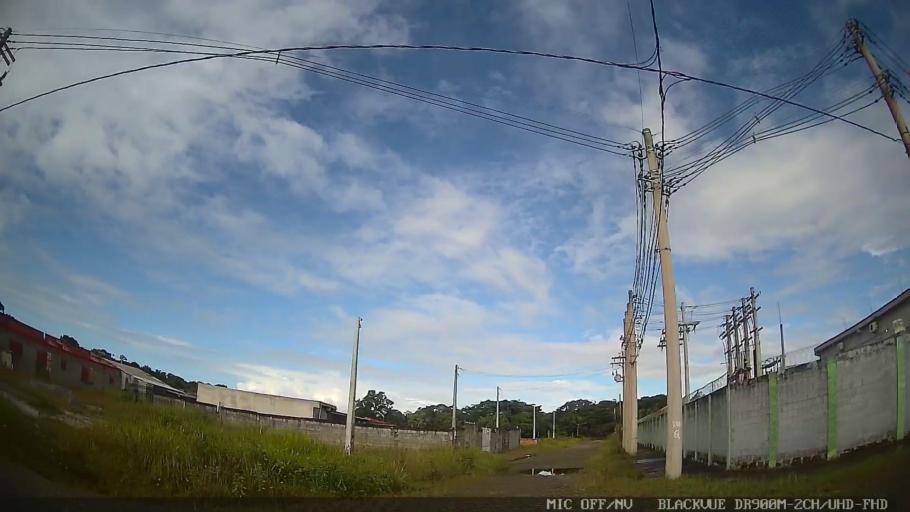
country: BR
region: Sao Paulo
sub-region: Itanhaem
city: Itanhaem
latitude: -24.2282
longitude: -46.8897
